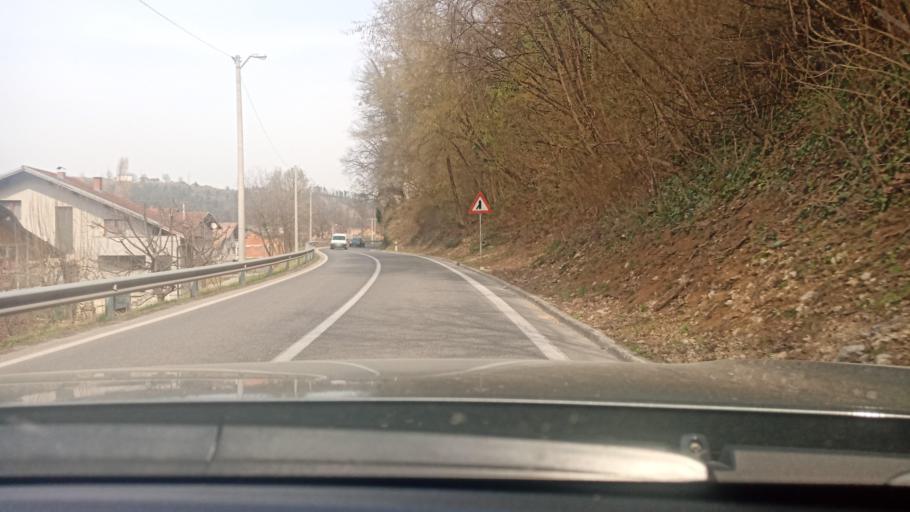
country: BA
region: Federation of Bosnia and Herzegovina
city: Bosanska Krupa
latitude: 44.8796
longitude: 16.1421
